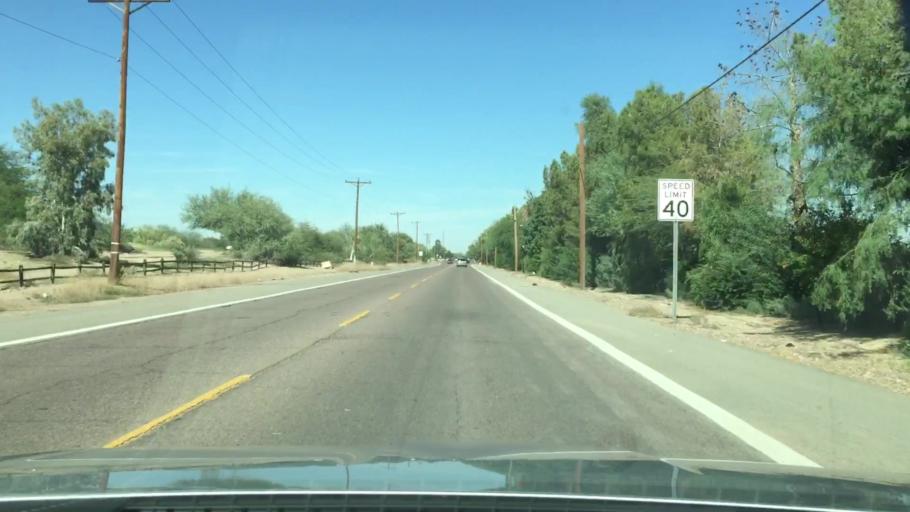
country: US
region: Arizona
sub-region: Maricopa County
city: Laveen
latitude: 33.3675
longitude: -112.1348
